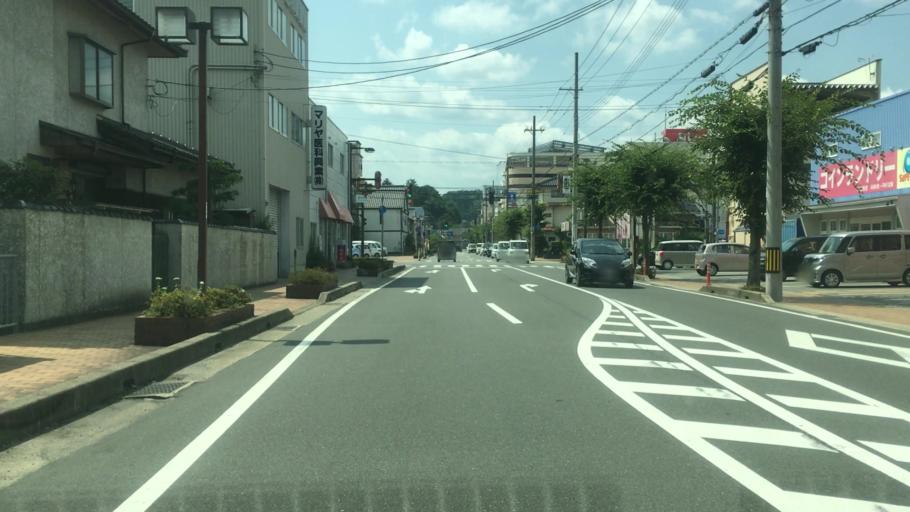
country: JP
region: Hyogo
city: Toyooka
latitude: 35.5475
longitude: 134.8156
